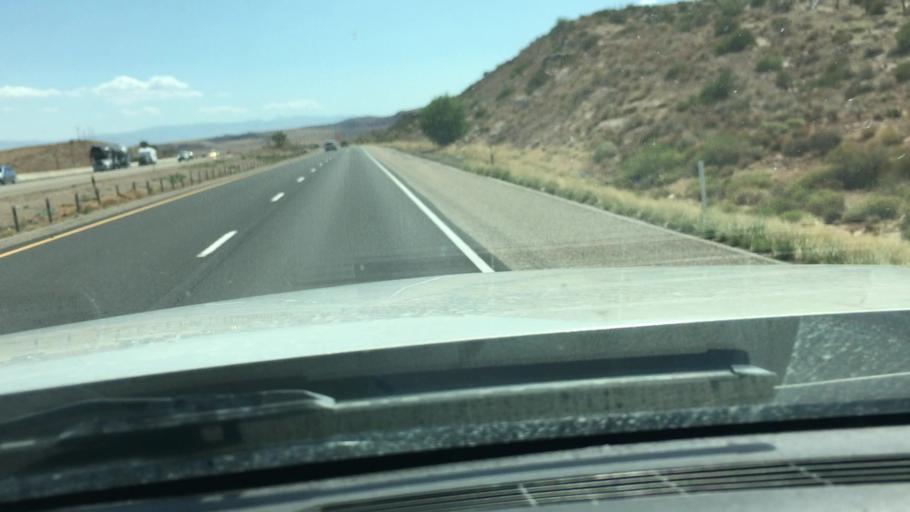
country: US
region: Utah
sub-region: Washington County
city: Toquerville
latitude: 37.2225
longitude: -113.3827
